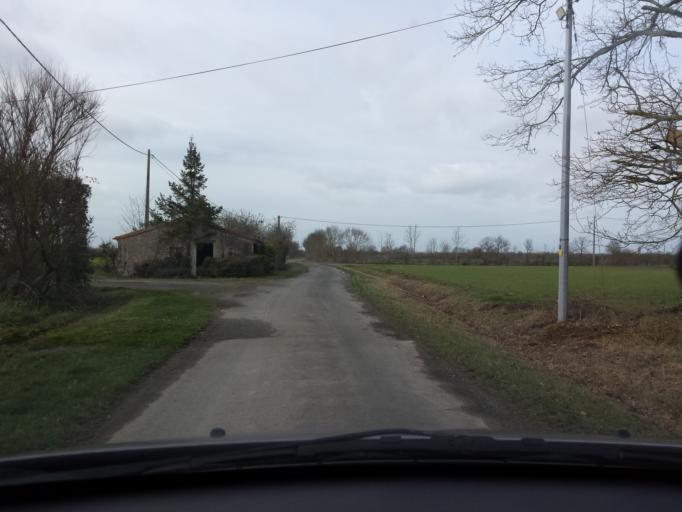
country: FR
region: Pays de la Loire
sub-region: Departement de la Vendee
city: Les Essarts
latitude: 46.7615
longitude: -1.2639
